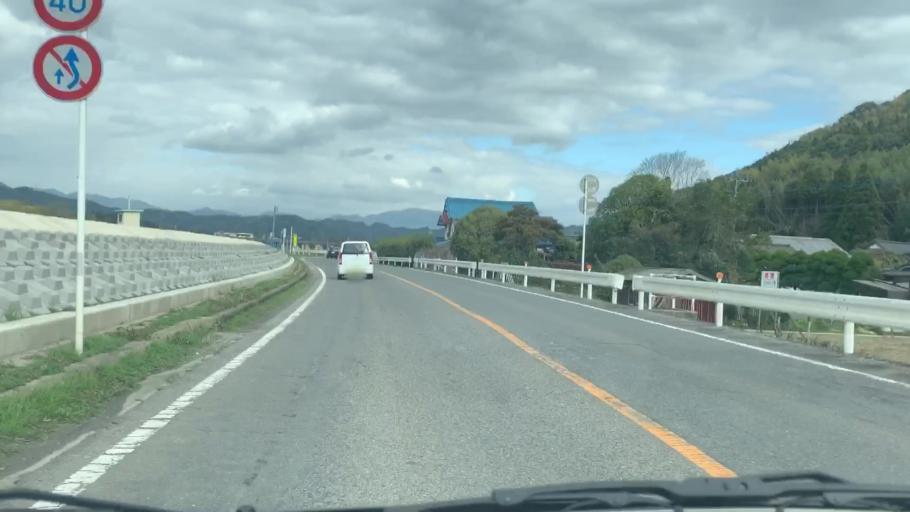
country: JP
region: Saga Prefecture
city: Takeocho-takeo
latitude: 33.2038
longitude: 130.0547
